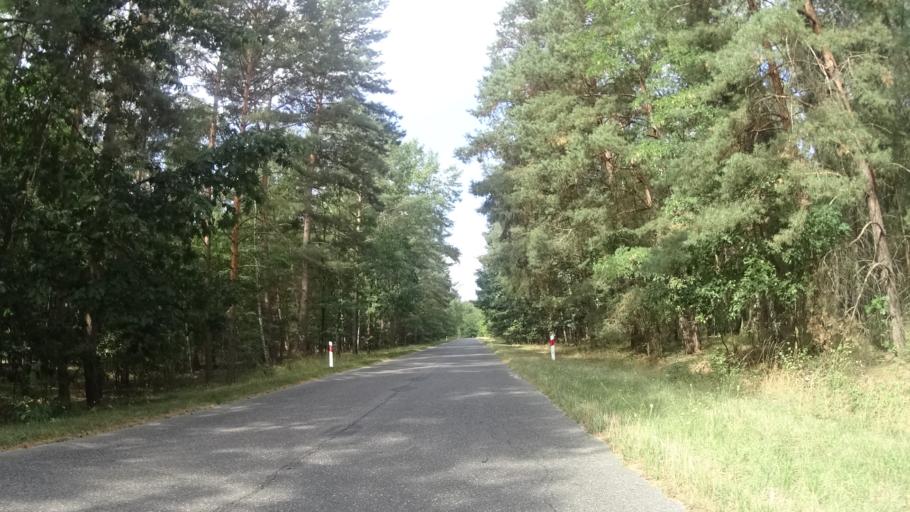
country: PL
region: Lubusz
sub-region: Powiat zarski
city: Leknica
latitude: 51.5419
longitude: 14.7809
